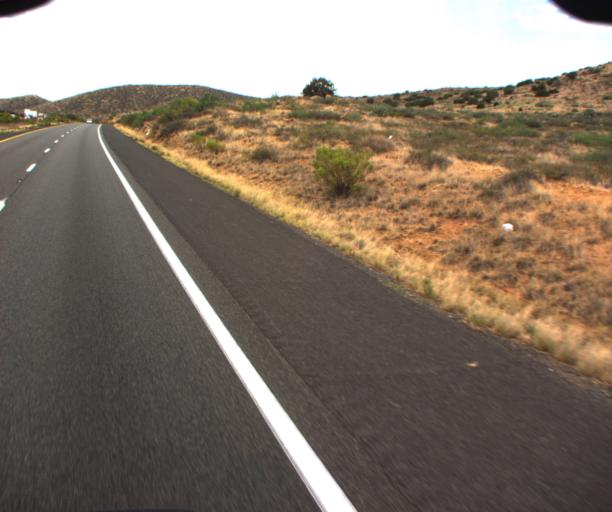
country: US
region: Arizona
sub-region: Yavapai County
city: Cordes Lakes
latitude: 34.3116
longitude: -112.1255
